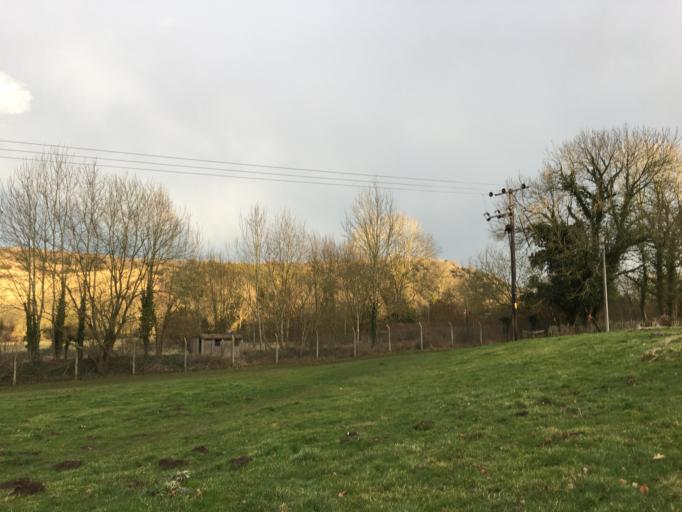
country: GB
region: England
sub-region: Surrey
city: Mickleham
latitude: 51.2556
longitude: -0.3297
